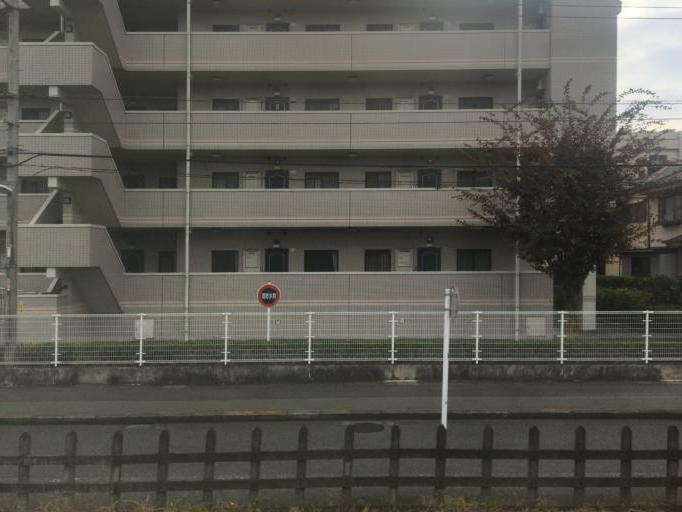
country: JP
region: Tokyo
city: Hino
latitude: 35.7055
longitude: 139.3870
